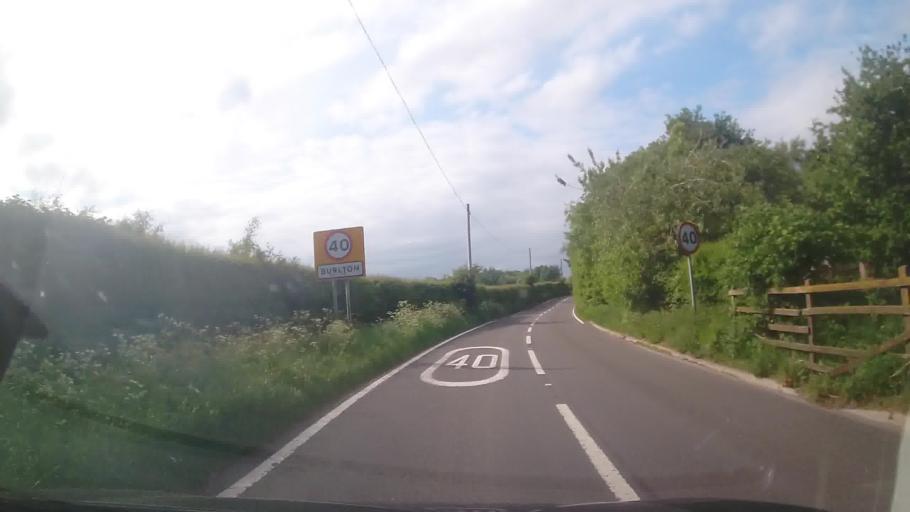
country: GB
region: England
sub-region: Shropshire
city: Petton
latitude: 52.8264
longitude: -2.8049
